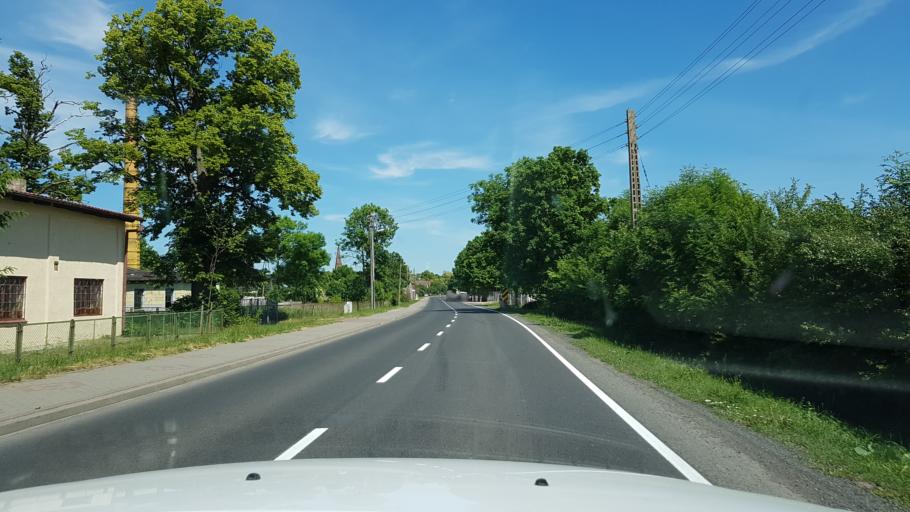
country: PL
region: West Pomeranian Voivodeship
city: Trzcinsko Zdroj
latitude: 52.9632
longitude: 14.5974
